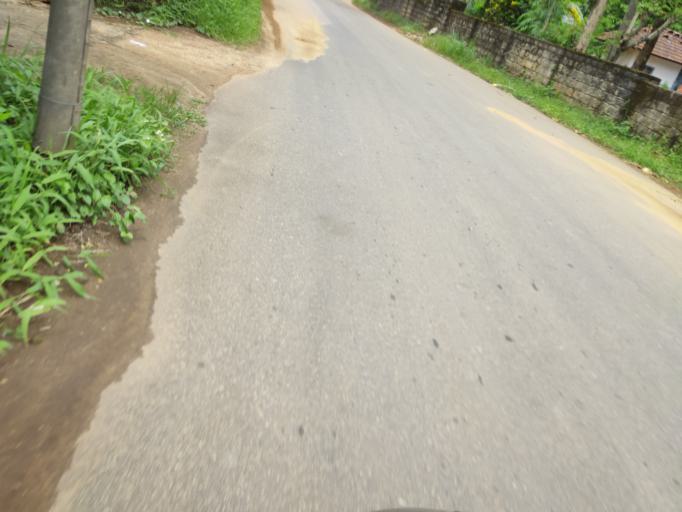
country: IN
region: Kerala
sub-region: Malappuram
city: Manjeri
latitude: 11.2047
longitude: 76.2596
